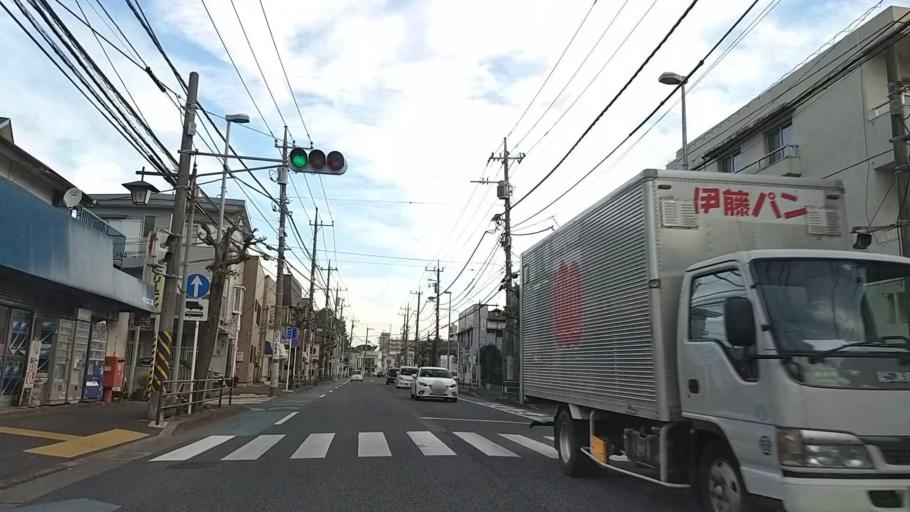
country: JP
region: Kanagawa
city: Atsugi
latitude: 35.4344
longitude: 139.3675
